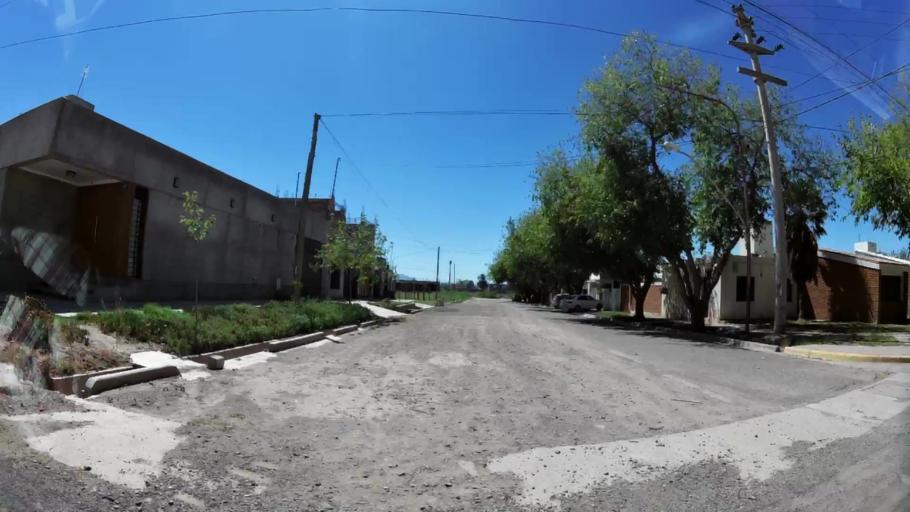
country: AR
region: Mendoza
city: Las Heras
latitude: -32.8485
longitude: -68.8502
